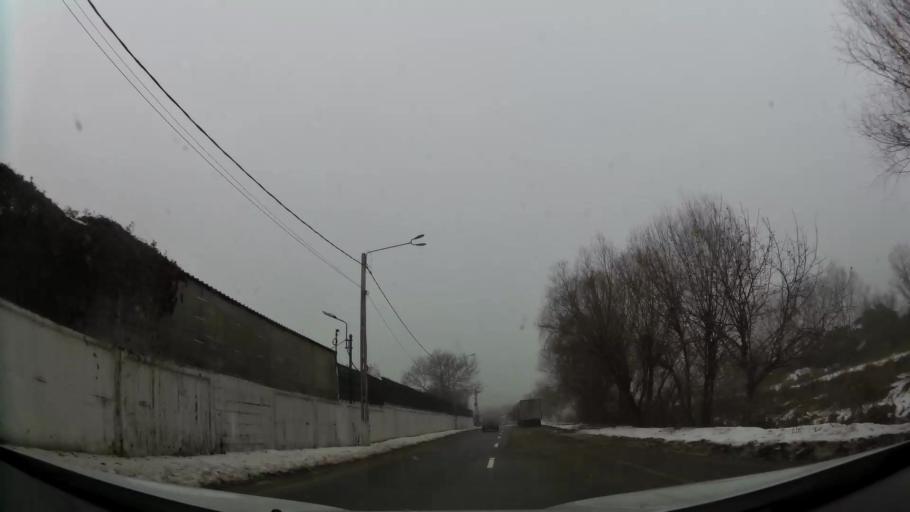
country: RO
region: Ilfov
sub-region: Comuna Chiajna
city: Chiajna
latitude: 44.4646
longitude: 25.9770
